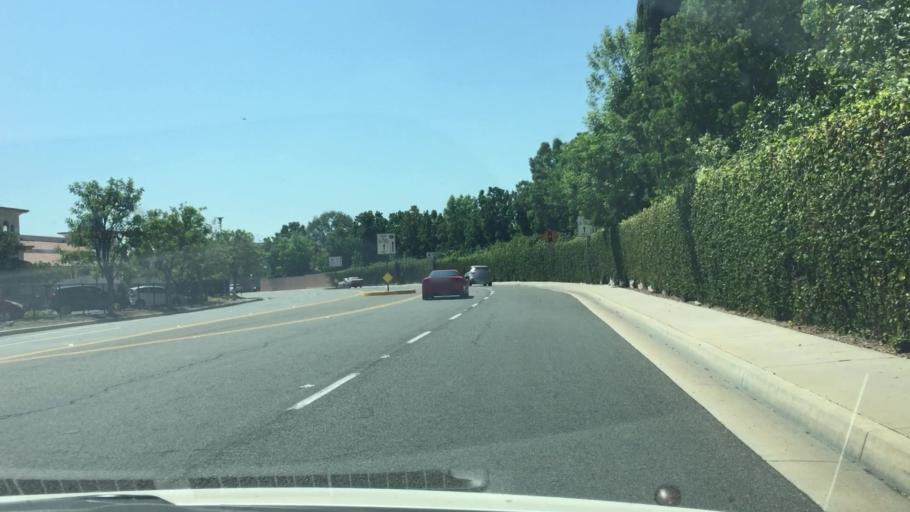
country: US
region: California
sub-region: Orange County
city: Laguna Hills
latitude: 33.6166
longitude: -117.7114
